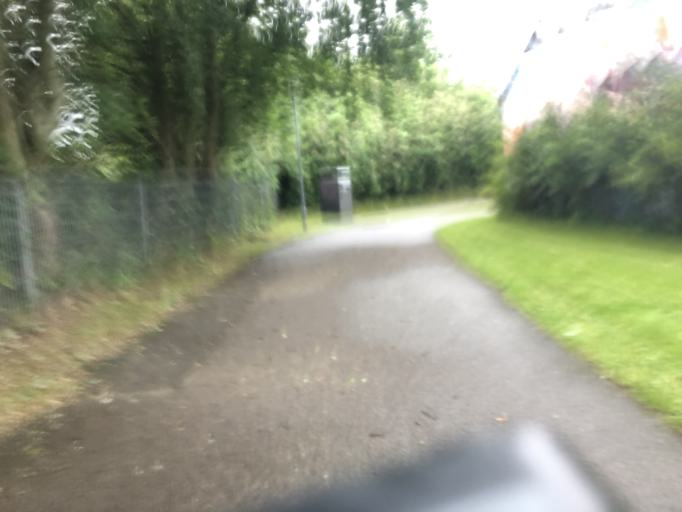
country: DK
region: Capital Region
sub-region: Gladsaxe Municipality
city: Buddinge
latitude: 55.7478
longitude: 12.4909
